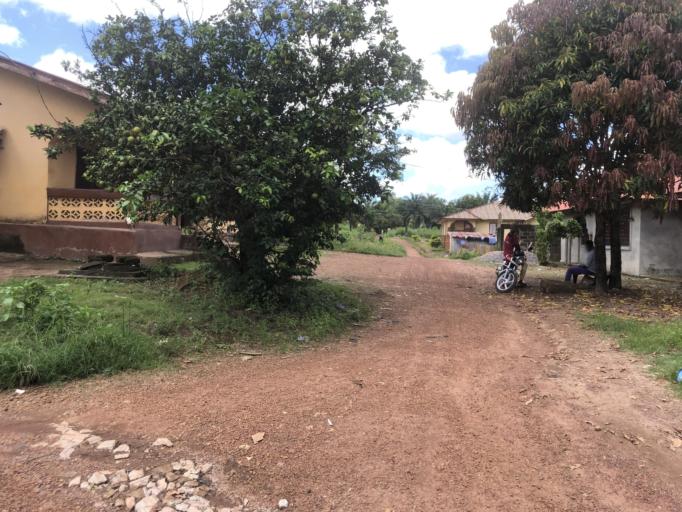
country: SL
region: Northern Province
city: Makeni
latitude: 8.8609
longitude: -12.0448
